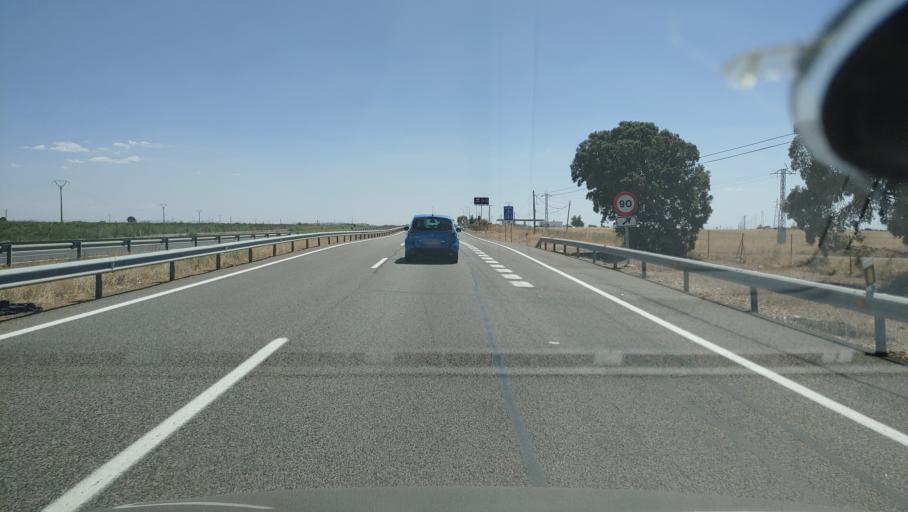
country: ES
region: Castille-La Mancha
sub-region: Provincia de Ciudad Real
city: Villarta de San Juan
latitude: 39.1854
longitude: -3.4001
